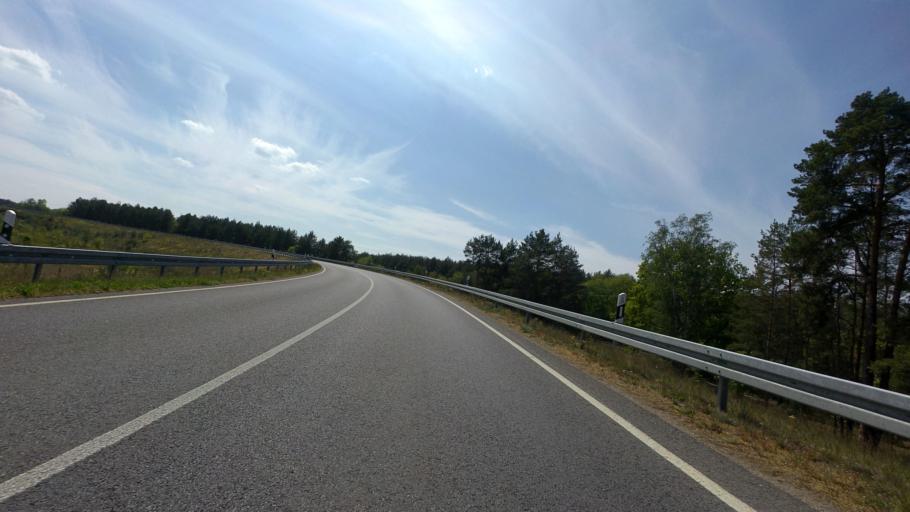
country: DE
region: Brandenburg
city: Cottbus
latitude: 51.7894
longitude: 14.3735
